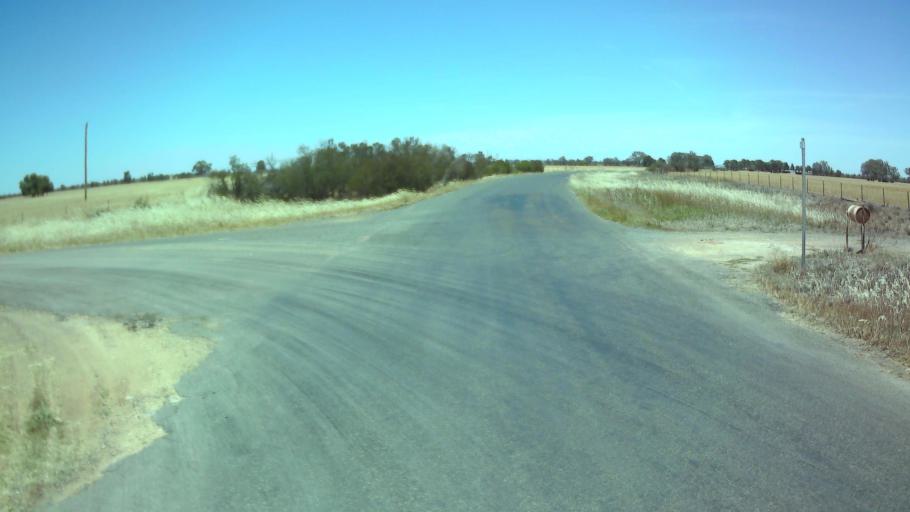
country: AU
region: New South Wales
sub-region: Weddin
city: Grenfell
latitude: -34.0401
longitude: 147.7893
